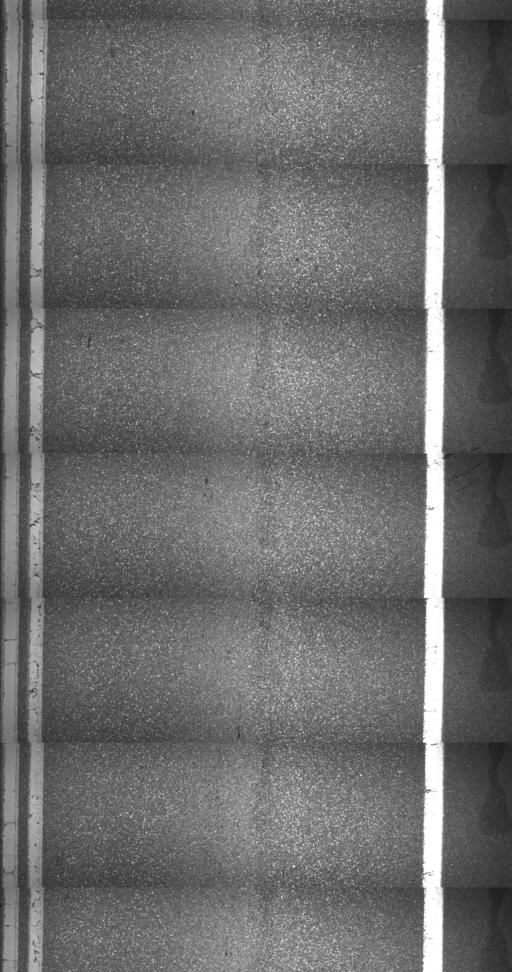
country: US
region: Vermont
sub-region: Windsor County
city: Windsor
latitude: 43.4260
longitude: -72.4776
